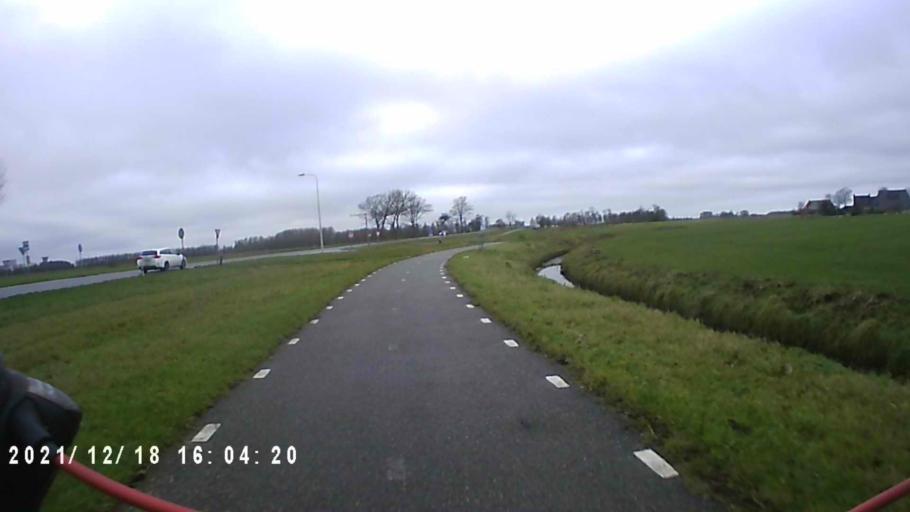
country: NL
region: Friesland
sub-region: Gemeente Dongeradeel
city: Anjum
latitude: 53.3517
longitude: 6.0780
